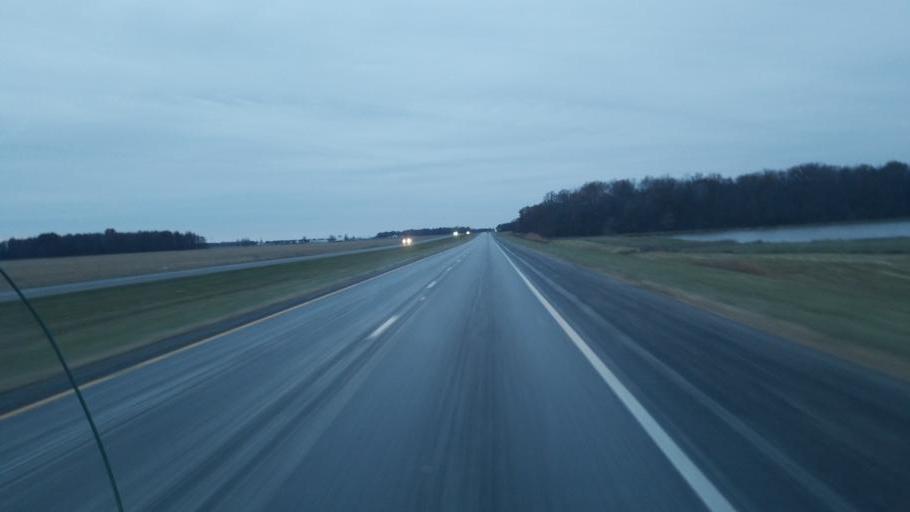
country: US
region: Ohio
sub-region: Hardin County
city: Ada
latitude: 40.8263
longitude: -83.7663
